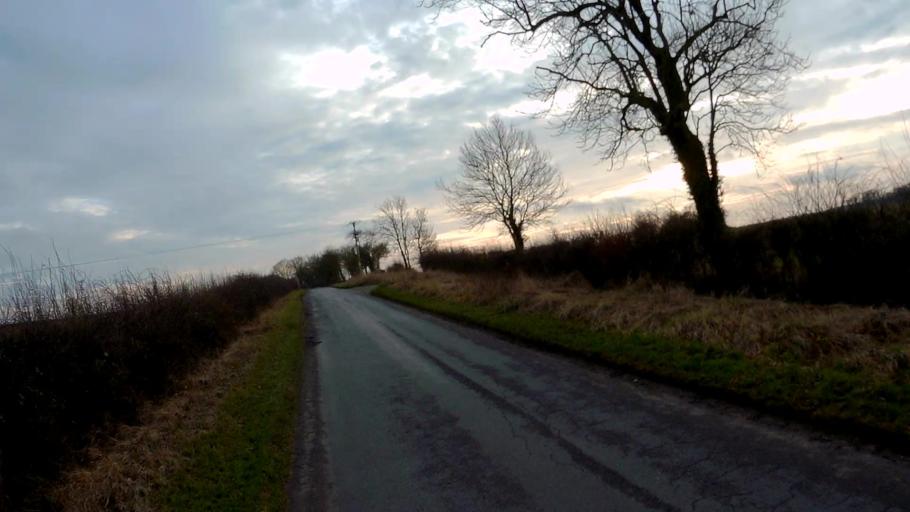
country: GB
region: England
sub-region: Lincolnshire
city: Bourne
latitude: 52.8297
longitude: -0.4405
